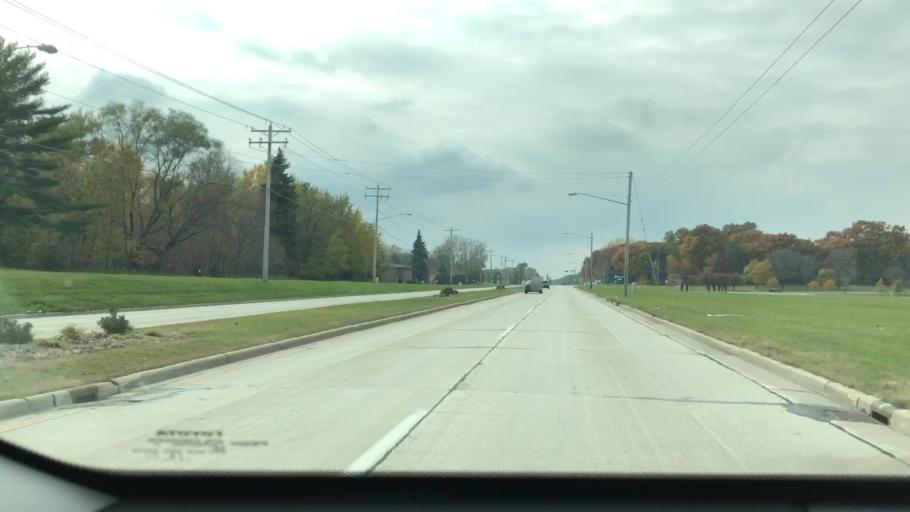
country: US
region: Wisconsin
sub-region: Brown County
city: Howard
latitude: 44.5240
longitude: -88.1053
